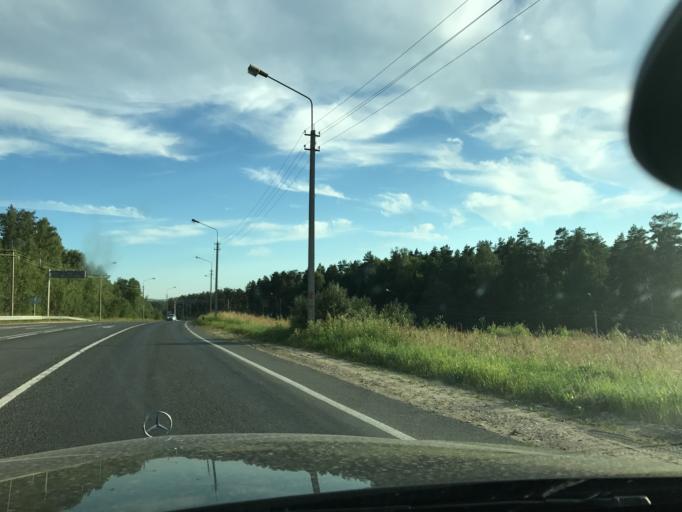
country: RU
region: Vladimir
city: Kommunar
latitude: 56.0557
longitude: 40.4397
